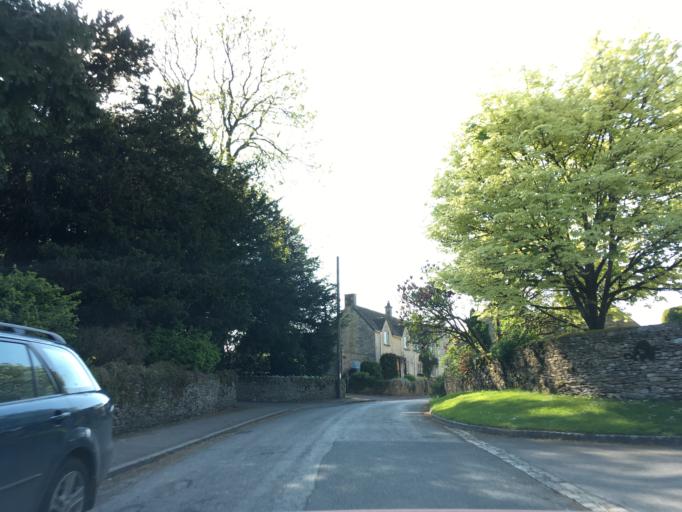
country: GB
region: England
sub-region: Gloucestershire
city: Nailsworth
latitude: 51.6649
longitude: -2.2646
